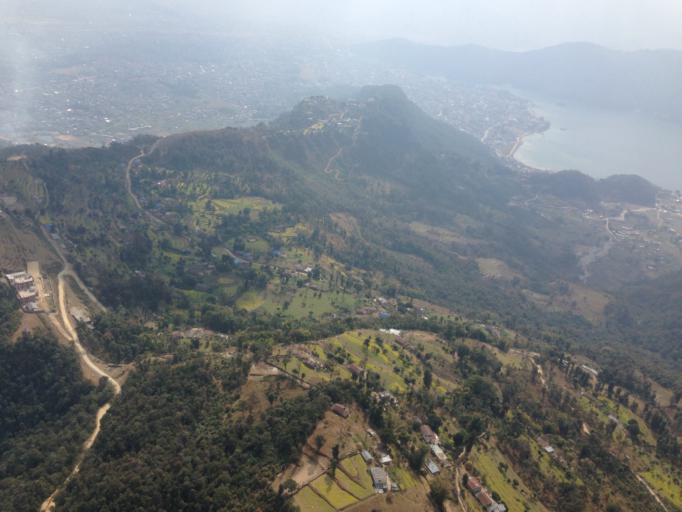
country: NP
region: Western Region
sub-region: Gandaki Zone
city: Pokhara
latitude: 28.2438
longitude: 83.9619
